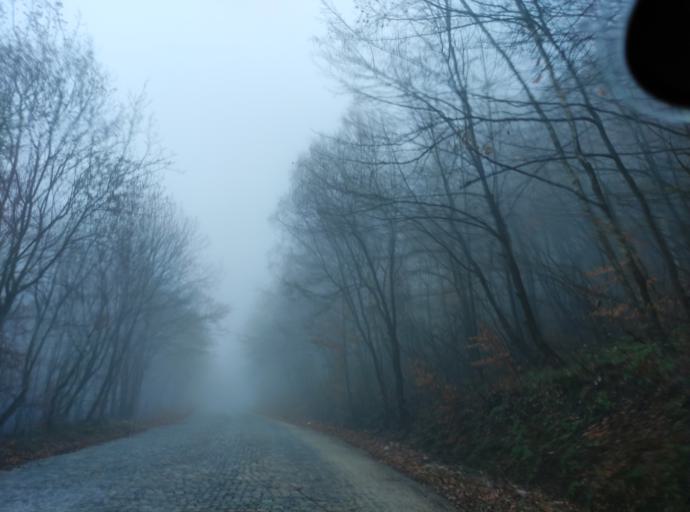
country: BG
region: Sofia-Capital
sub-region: Stolichna Obshtina
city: Sofia
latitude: 42.6255
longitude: 23.2916
